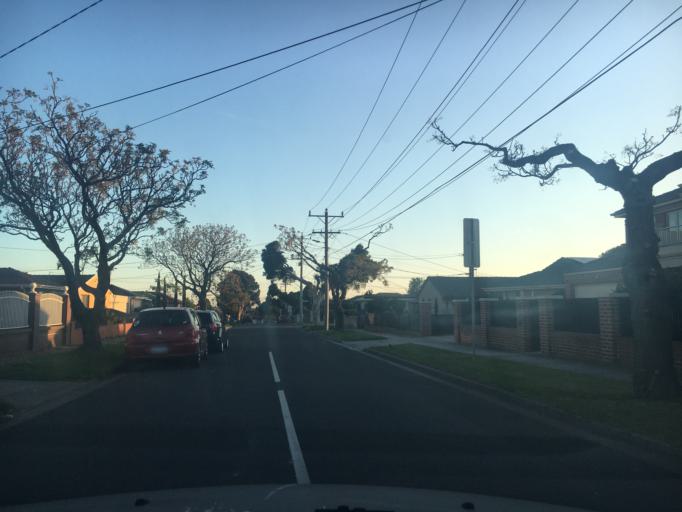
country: AU
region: Victoria
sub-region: Greater Dandenong
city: Springvale
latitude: -37.9428
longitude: 145.1360
